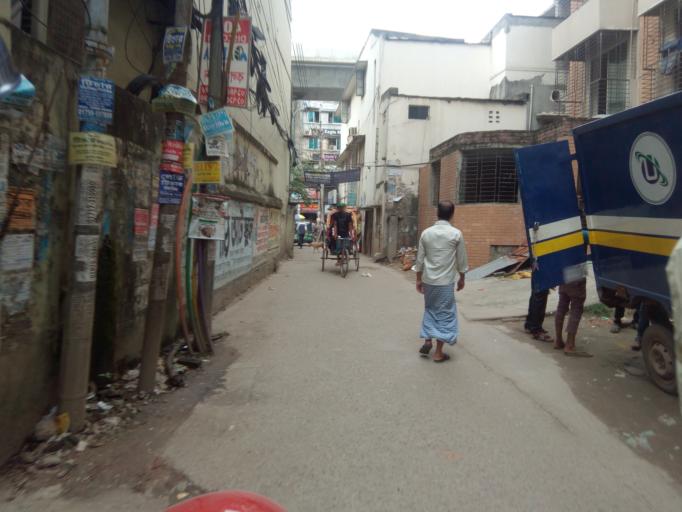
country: BD
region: Dhaka
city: Paltan
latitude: 23.7473
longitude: 90.4012
